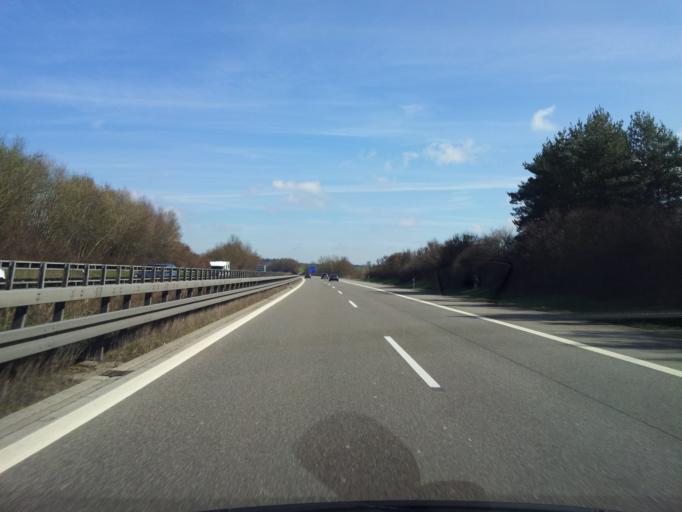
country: DE
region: Baden-Wuerttemberg
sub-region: Karlsruhe Region
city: Empfingen
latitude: 48.4232
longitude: 8.7390
